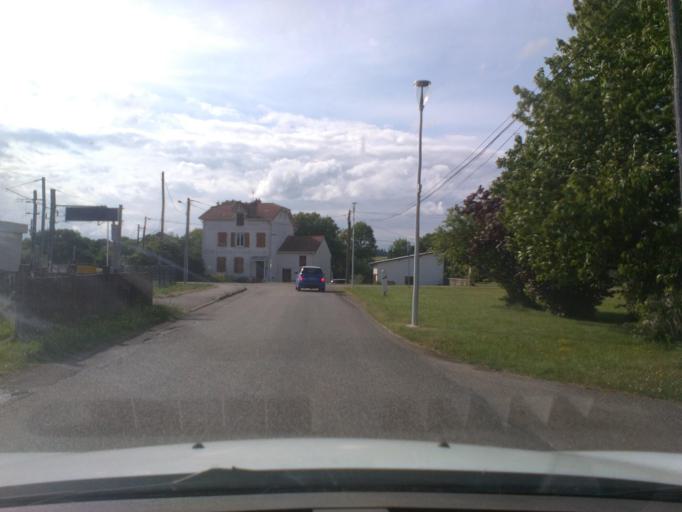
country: FR
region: Lorraine
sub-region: Departement de Meurthe-et-Moselle
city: Baccarat
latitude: 48.4913
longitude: 6.6966
